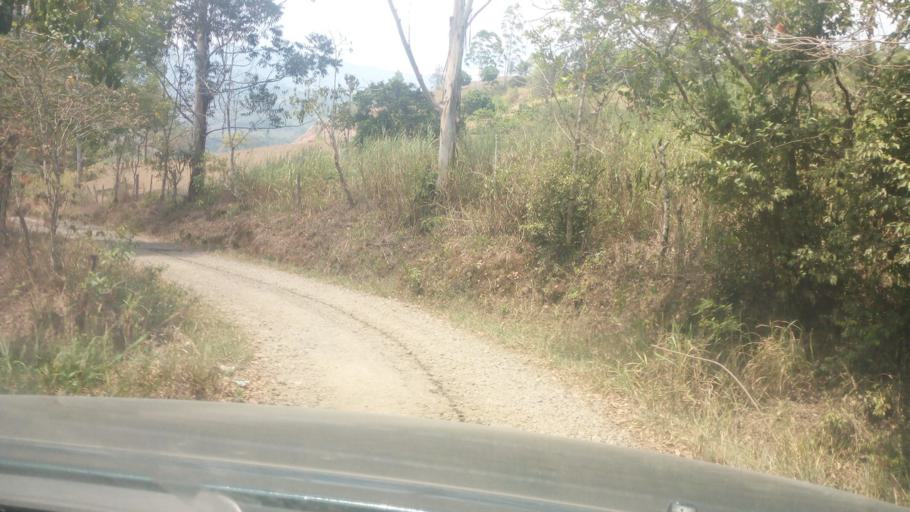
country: CO
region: Boyaca
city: Guateque
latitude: 4.9883
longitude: -73.4610
